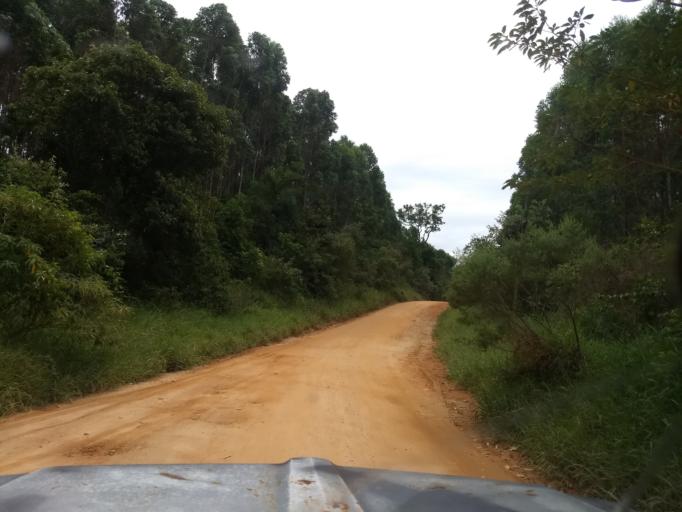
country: BR
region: Sao Paulo
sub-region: Cabreuva
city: Cabreuva
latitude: -23.3962
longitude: -47.1951
